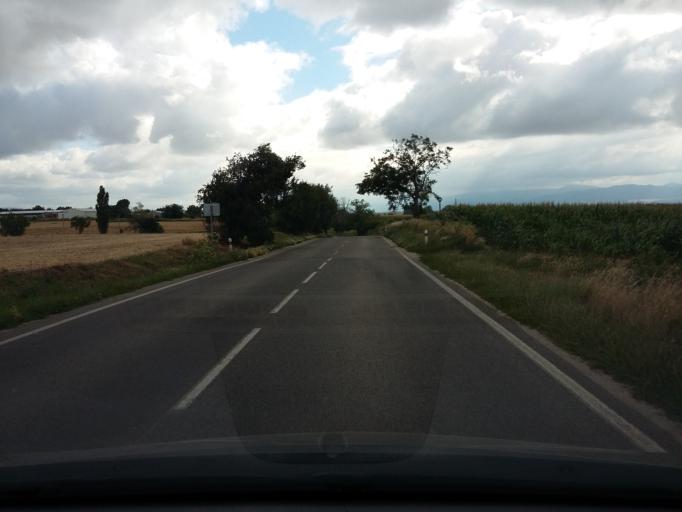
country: SK
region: Trnavsky
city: Vrbove
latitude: 48.6076
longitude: 17.7113
